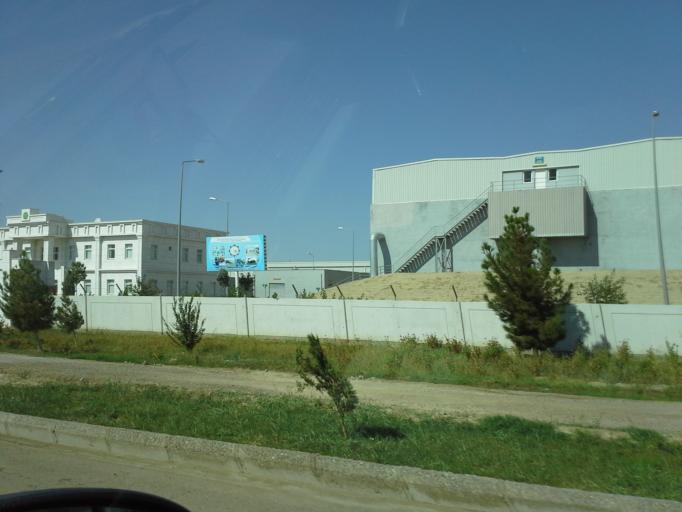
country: TM
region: Dasoguz
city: Dasoguz
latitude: 41.8100
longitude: 59.9958
